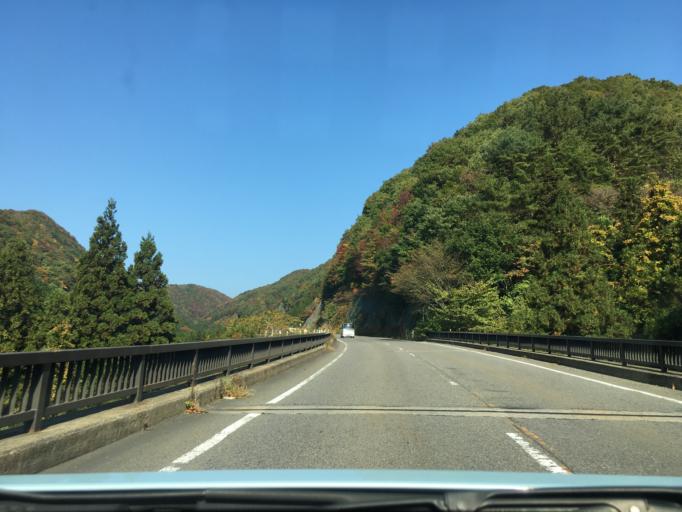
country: JP
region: Fukushima
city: Inawashiro
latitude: 37.3179
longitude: 140.1360
